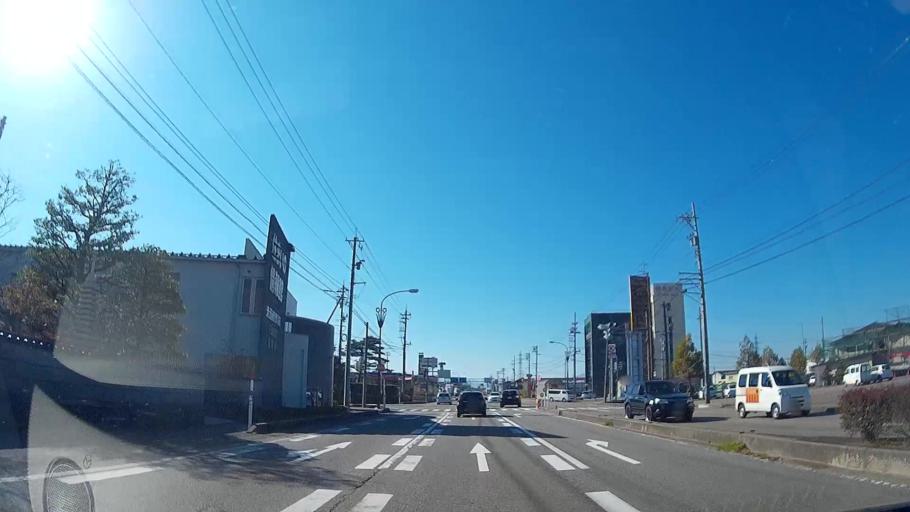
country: JP
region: Toyama
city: Nanto-shi
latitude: 36.6484
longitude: 136.9620
